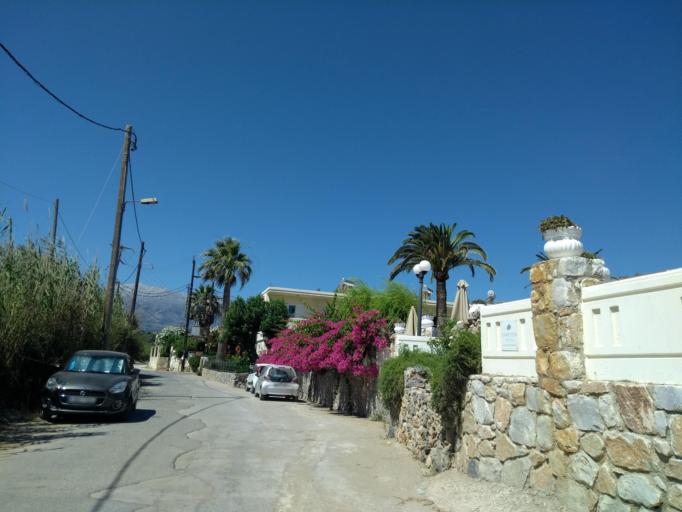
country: GR
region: Crete
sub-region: Nomos Chanias
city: Kalivai
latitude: 35.4617
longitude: 24.1602
